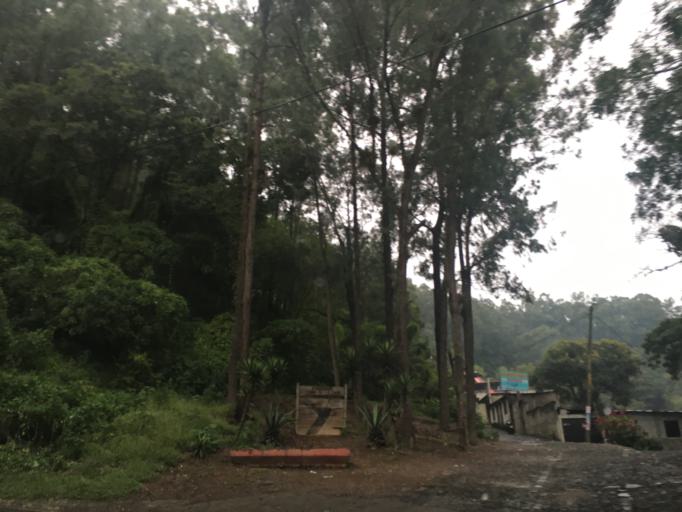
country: GT
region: Sacatepequez
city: Antigua Guatemala
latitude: 14.5683
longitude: -90.7270
